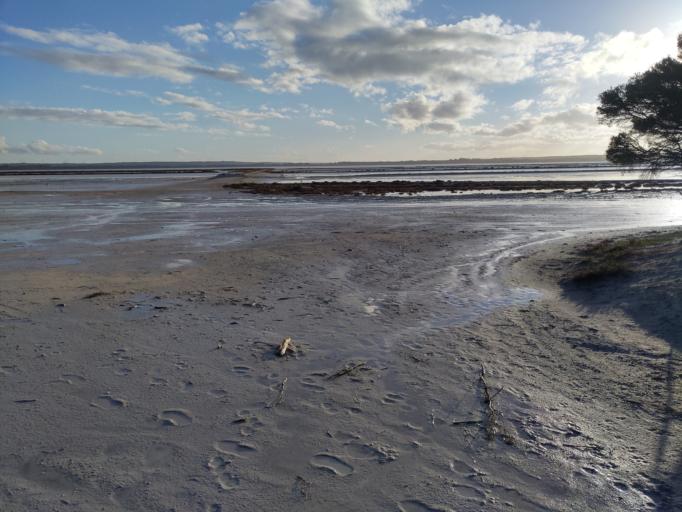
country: AU
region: Western Australia
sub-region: Esperance Shire
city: Nulsen
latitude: -33.8340
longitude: 121.8505
